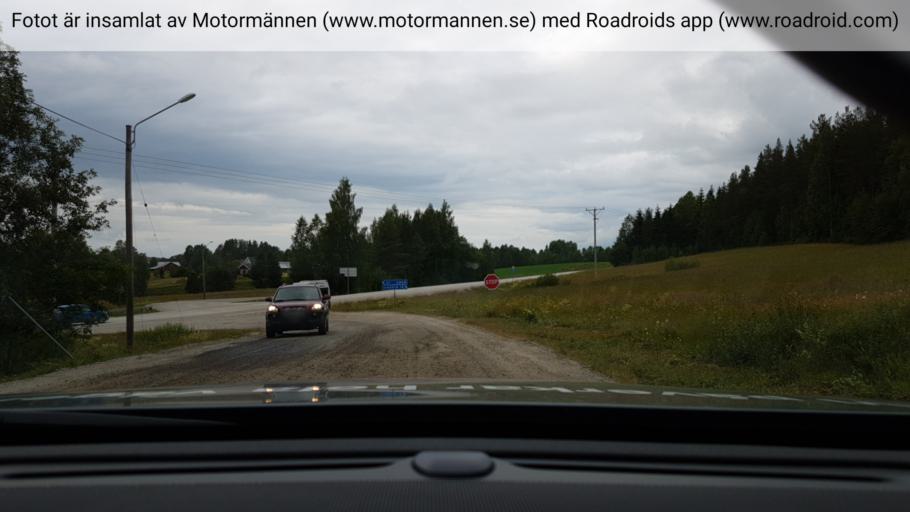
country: SE
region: Vaesterbotten
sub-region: Vannas Kommun
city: Vannasby
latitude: 64.1063
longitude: 19.9751
